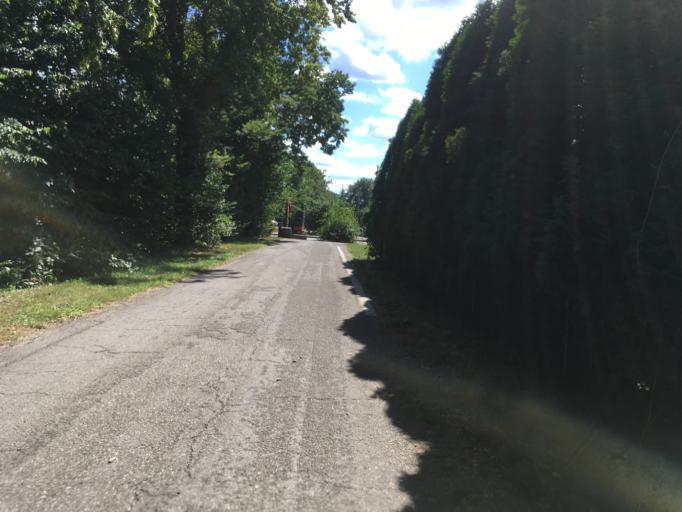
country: DE
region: Baden-Wuerttemberg
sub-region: Karlsruhe Region
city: Niefern-Oschelbronn
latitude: 48.9348
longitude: 8.8030
